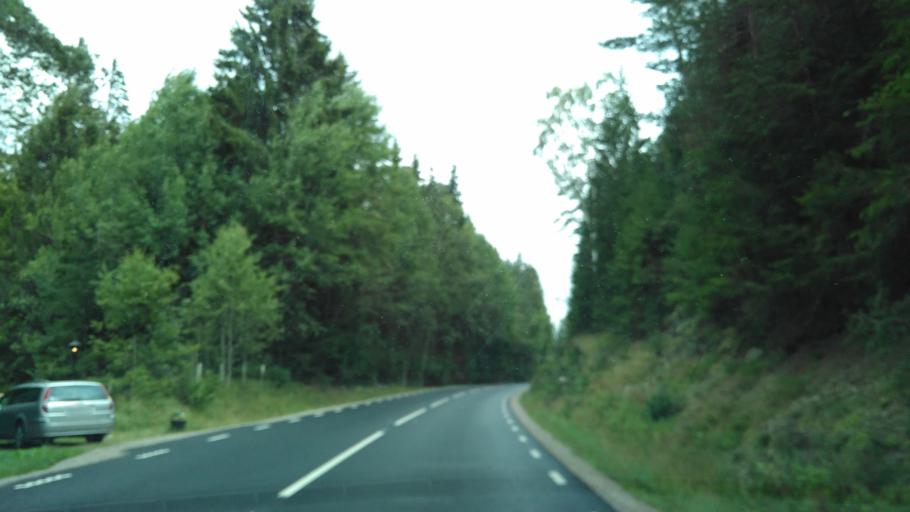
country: SE
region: Vaestra Goetaland
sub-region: Marks Kommun
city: Fritsla
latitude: 57.5915
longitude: 12.7497
